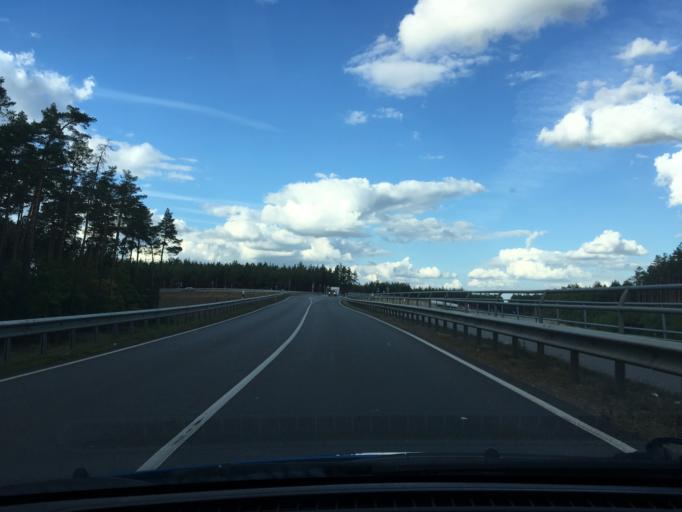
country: DE
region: Mecklenburg-Vorpommern
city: Ludwigslust
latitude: 53.3413
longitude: 11.5167
